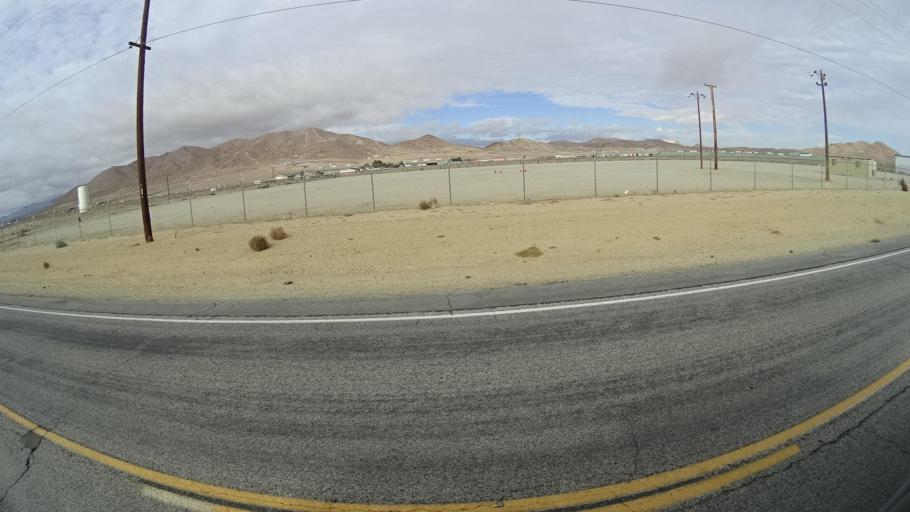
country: US
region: California
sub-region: Kern County
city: Rosamond
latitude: 34.8636
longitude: -118.2637
